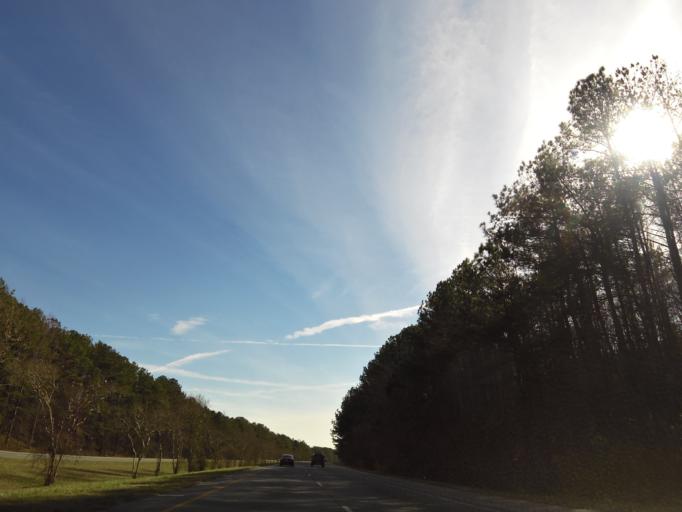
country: US
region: Georgia
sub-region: Harris County
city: Hamilton
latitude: 32.7325
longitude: -85.0186
